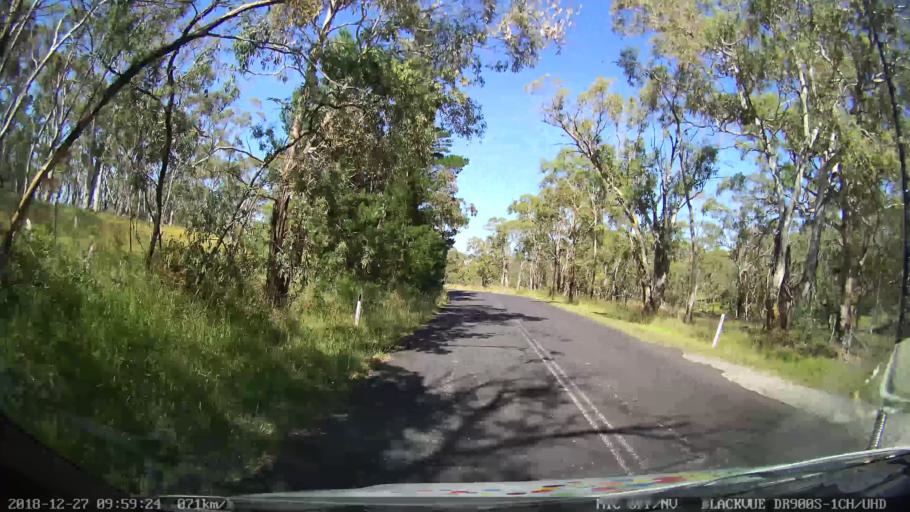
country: AU
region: New South Wales
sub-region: Lithgow
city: Portland
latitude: -33.4337
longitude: 149.9522
